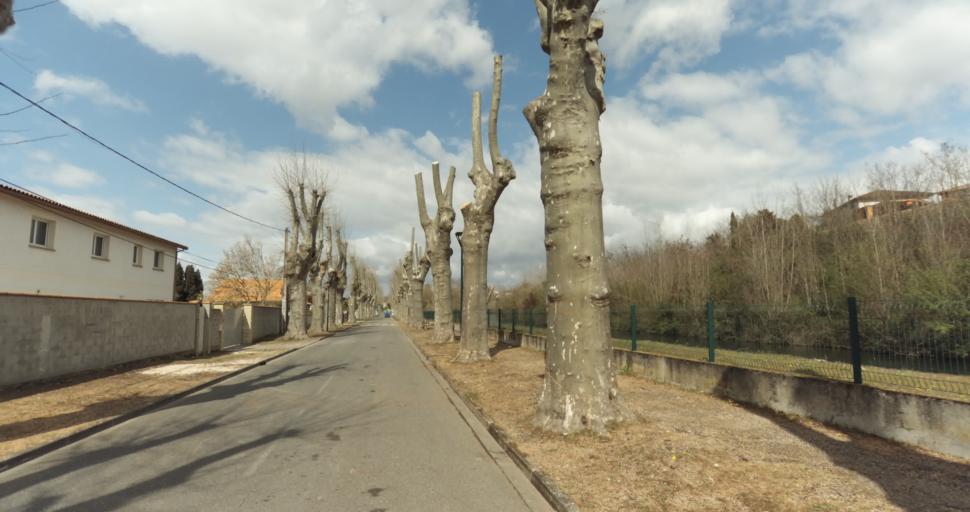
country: FR
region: Midi-Pyrenees
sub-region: Departement de la Haute-Garonne
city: Auterive
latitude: 43.3458
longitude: 1.4794
